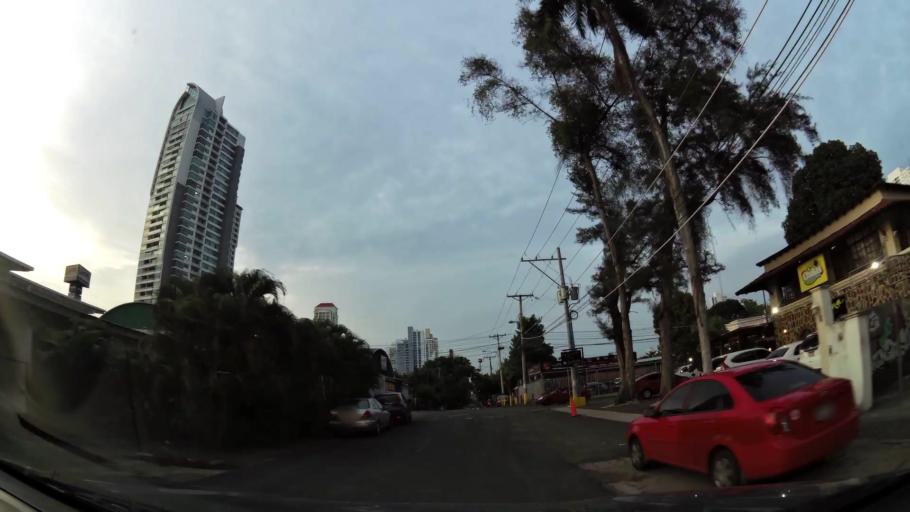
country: PA
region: Panama
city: Panama
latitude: 8.9875
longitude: -79.5096
